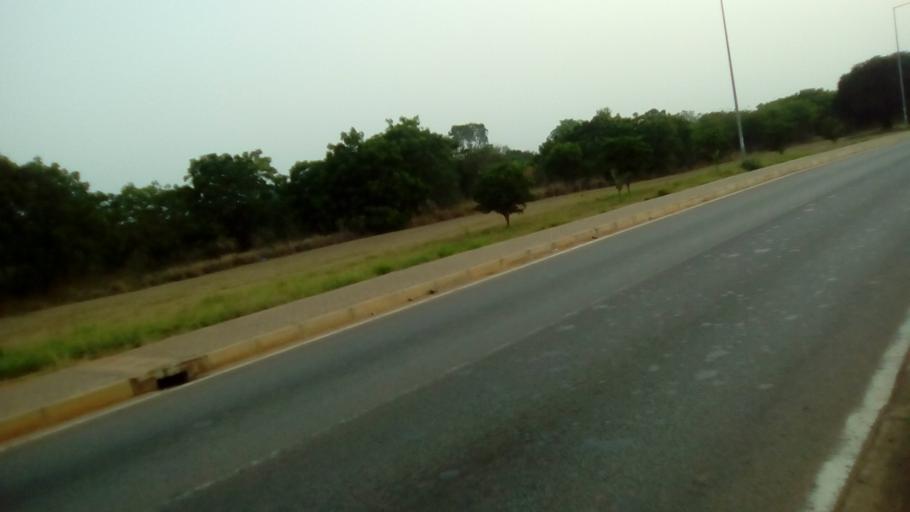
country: GH
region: Greater Accra
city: Medina Estates
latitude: 5.6403
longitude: -0.1825
